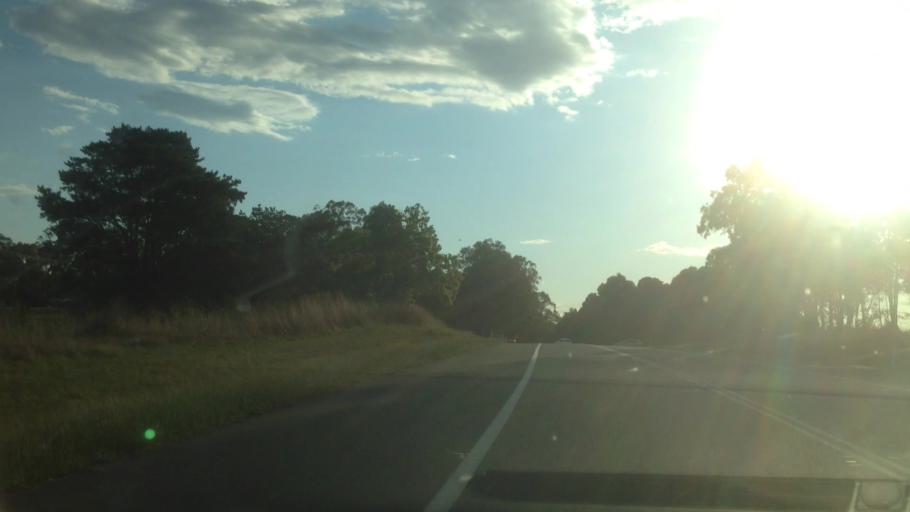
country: AU
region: New South Wales
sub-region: Cessnock
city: Heddon Greta
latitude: -32.8303
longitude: 151.5146
